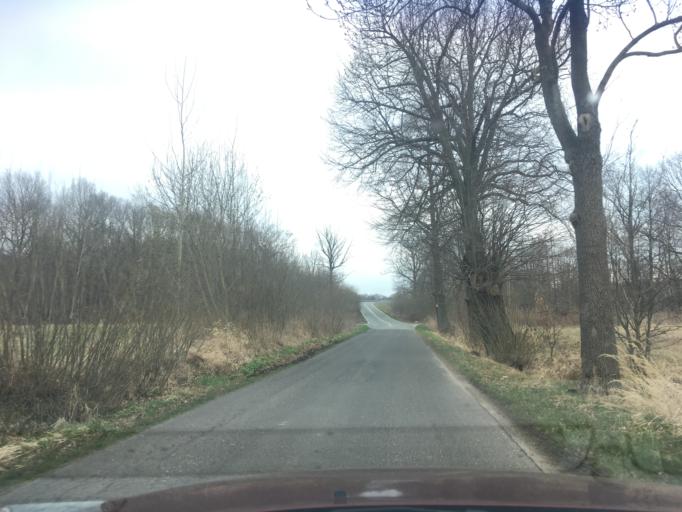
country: PL
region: Lower Silesian Voivodeship
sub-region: Powiat zgorzelecki
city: Lagow
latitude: 51.1743
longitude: 15.0438
